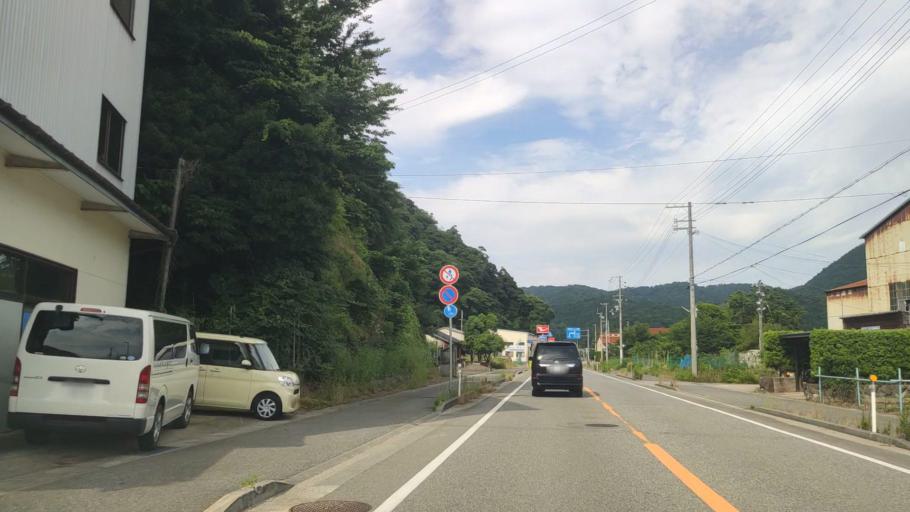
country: JP
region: Hyogo
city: Toyooka
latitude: 35.6426
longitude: 134.8316
